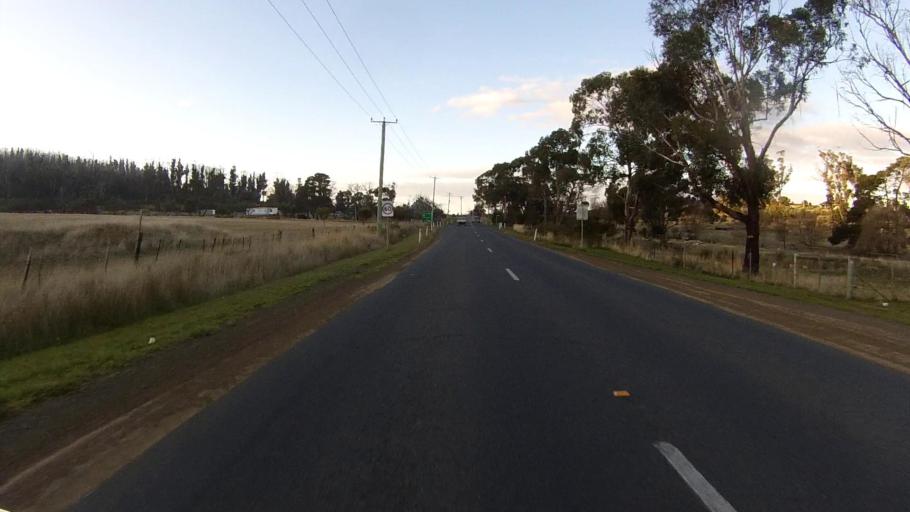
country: AU
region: Tasmania
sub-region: Sorell
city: Sorell
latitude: -42.8801
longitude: 147.8199
